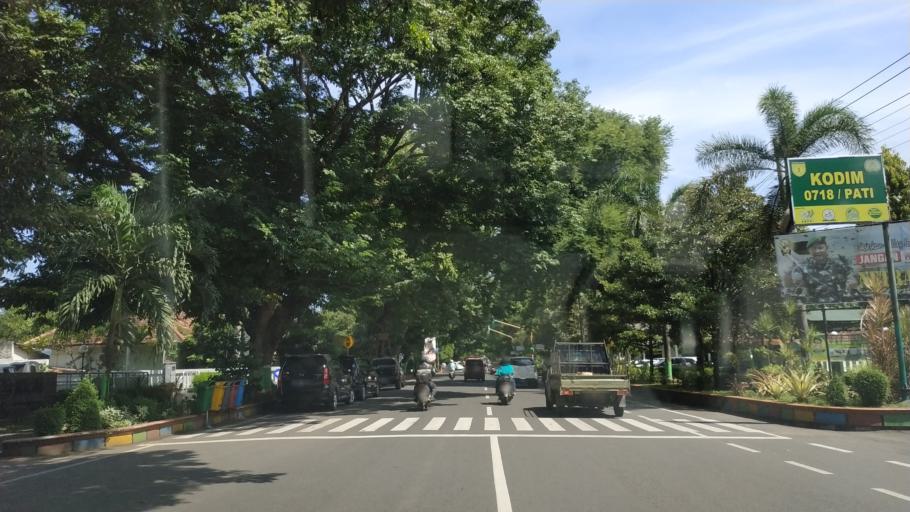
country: ID
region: Central Java
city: Pati
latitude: -6.7517
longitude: 111.0338
